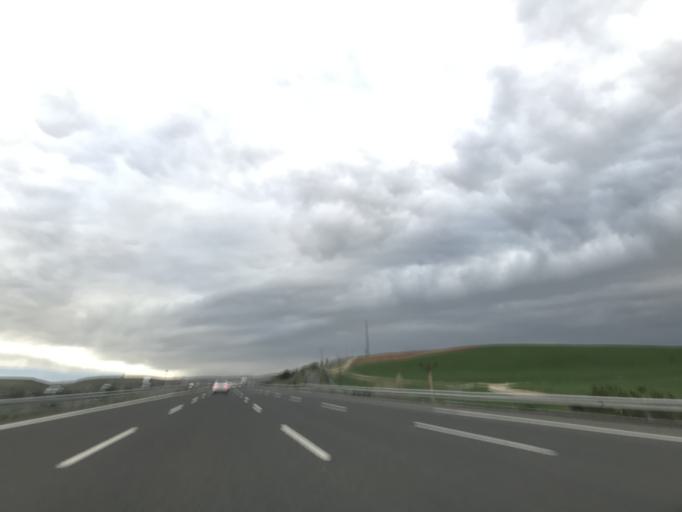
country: TR
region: Ankara
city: Etimesgut
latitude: 39.8318
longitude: 32.6458
